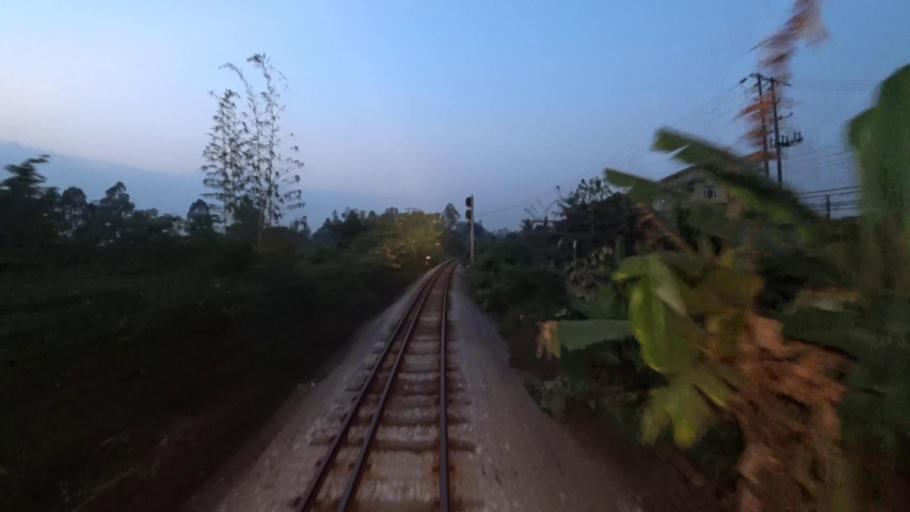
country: VN
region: Ha Noi
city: Soc Son
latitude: 21.2487
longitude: 105.8617
